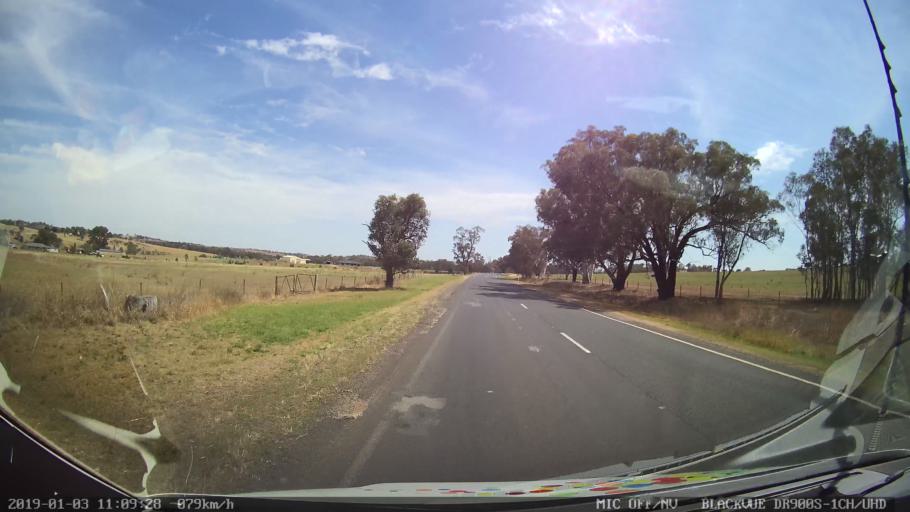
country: AU
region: New South Wales
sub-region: Young
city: Young
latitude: -34.2380
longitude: 148.2554
